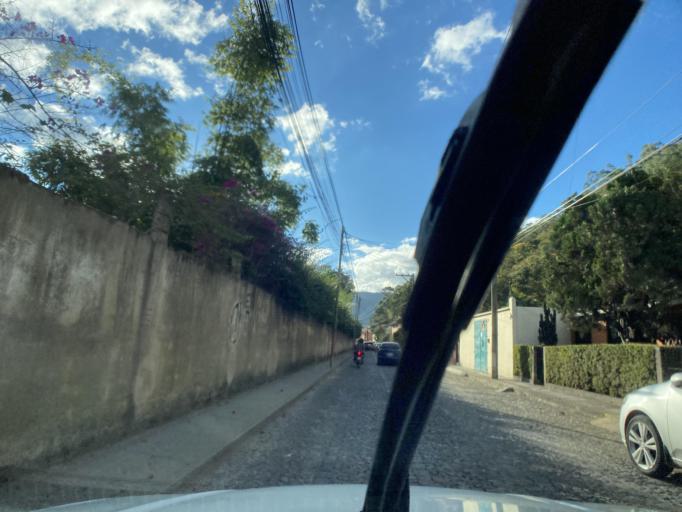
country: GT
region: Sacatepequez
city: Antigua Guatemala
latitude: 14.5629
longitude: -90.7307
